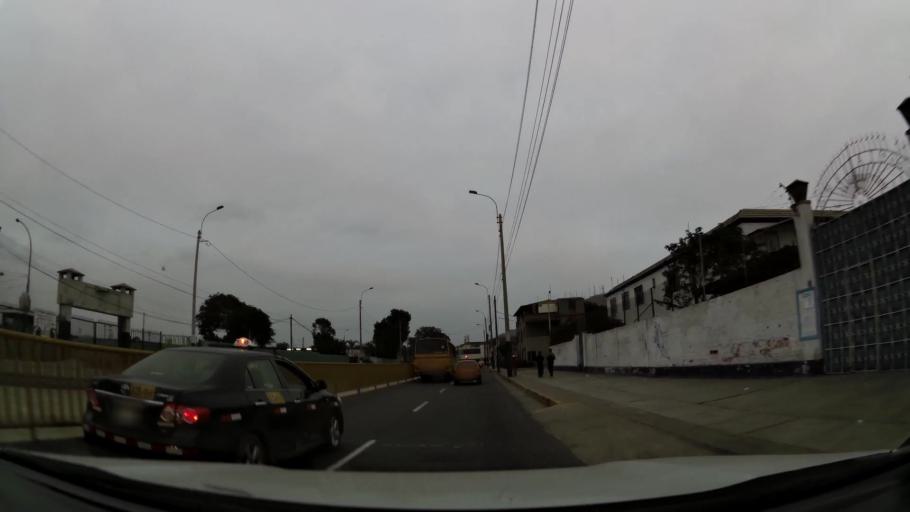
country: PE
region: Lima
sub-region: Lima
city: Surco
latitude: -12.1665
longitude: -77.0196
